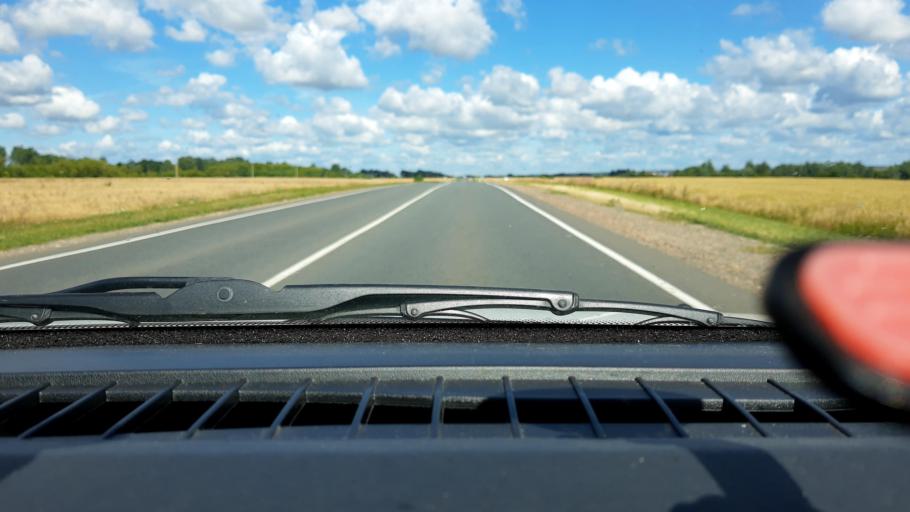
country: RU
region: Nizjnij Novgorod
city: Shatki
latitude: 55.2540
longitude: 43.9837
